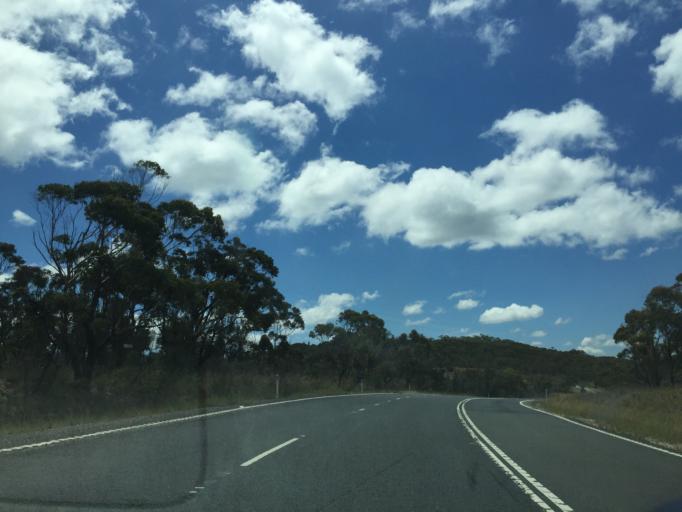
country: AU
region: New South Wales
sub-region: Blue Mountains Municipality
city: Blackheath
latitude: -33.5306
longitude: 150.3090
